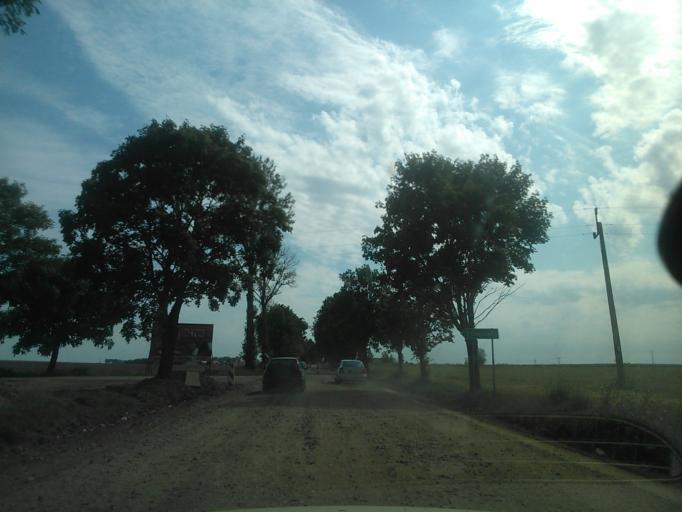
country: PL
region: Warmian-Masurian Voivodeship
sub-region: Powiat dzialdowski
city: Ilowo -Osada
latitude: 53.2043
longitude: 20.2400
